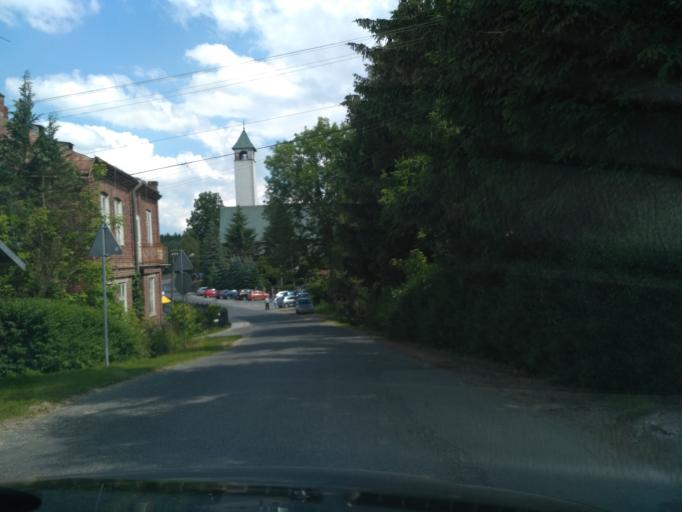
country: PL
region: Subcarpathian Voivodeship
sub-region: Powiat rzeszowski
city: Blazowa
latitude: 49.8580
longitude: 22.0682
